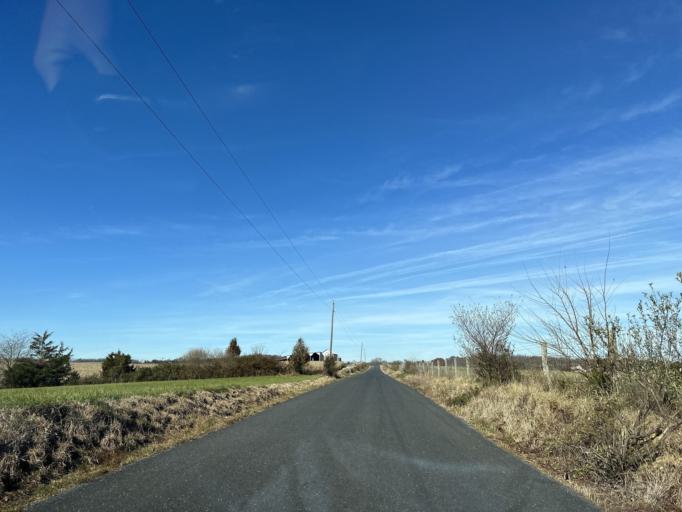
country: US
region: Virginia
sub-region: Augusta County
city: Weyers Cave
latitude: 38.2672
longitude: -78.9282
